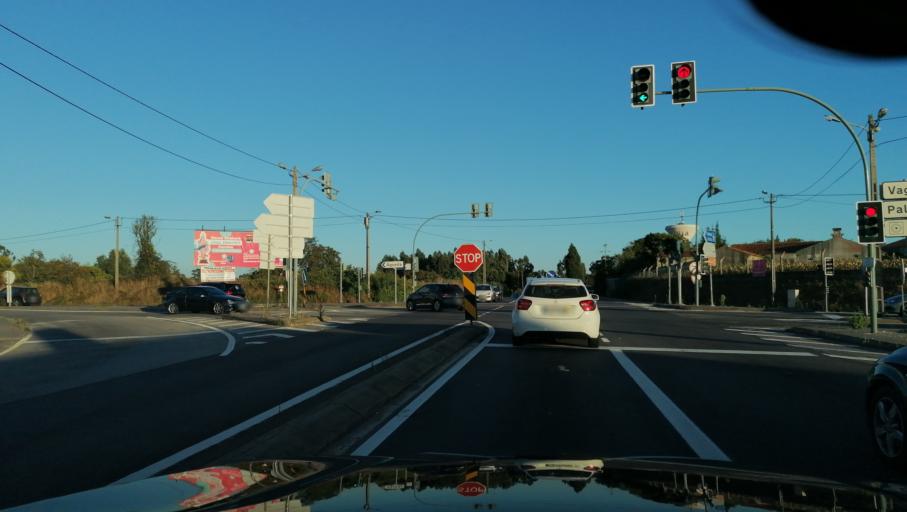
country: PT
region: Aveiro
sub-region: Oliveira do Bairro
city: Oia
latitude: 40.5432
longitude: -8.5330
